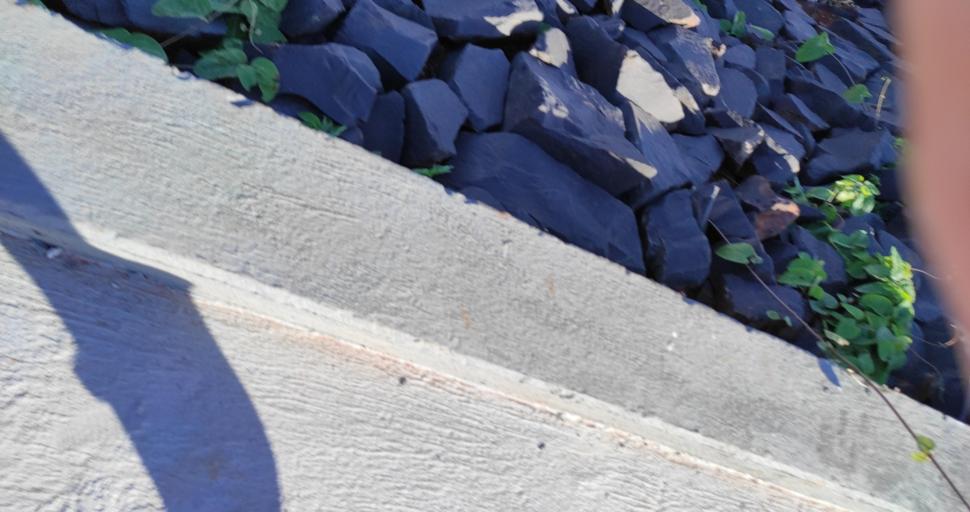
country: AR
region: Misiones
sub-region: Departamento de Capital
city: Posadas
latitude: -27.3643
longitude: -55.9576
